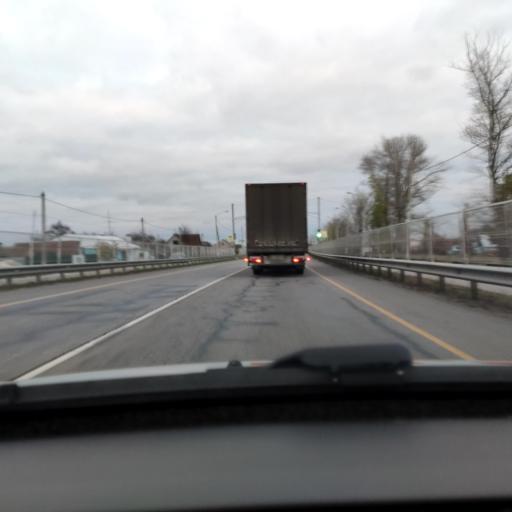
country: RU
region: Lipetsk
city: Khlevnoye
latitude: 52.2638
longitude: 39.1596
